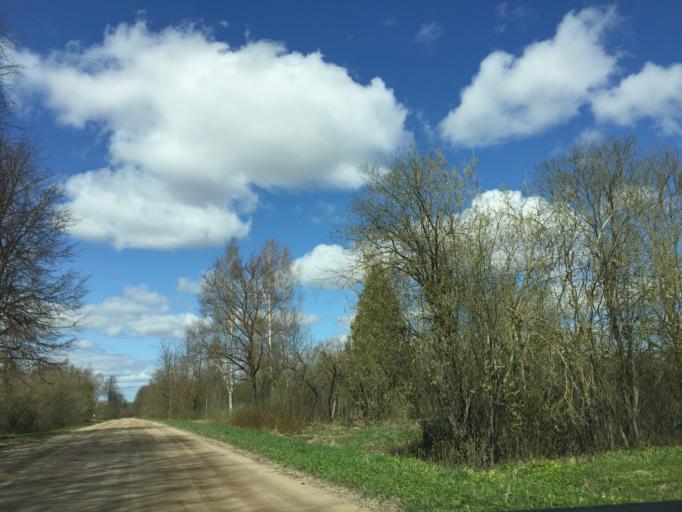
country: LV
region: Vilanu
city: Vilani
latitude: 56.6530
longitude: 27.1274
